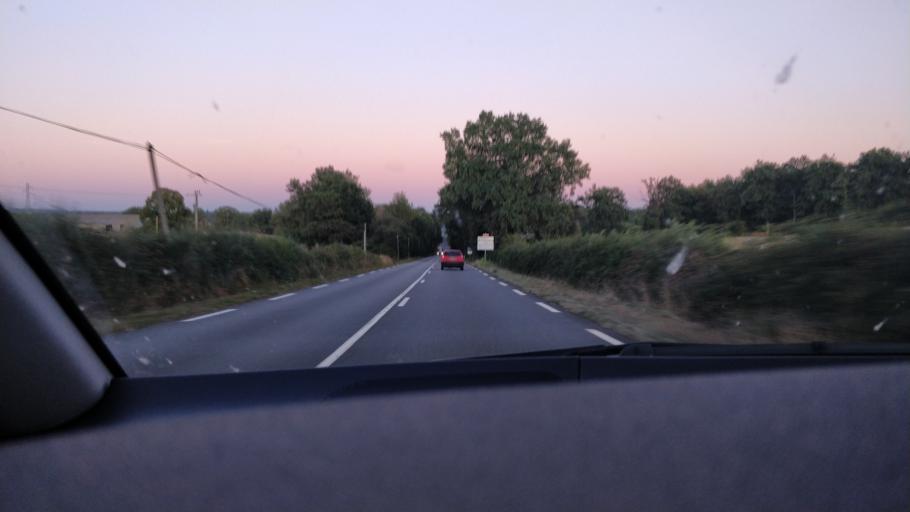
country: FR
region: Poitou-Charentes
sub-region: Departement de la Charente
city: Exideuil
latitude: 45.8793
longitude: 0.6244
